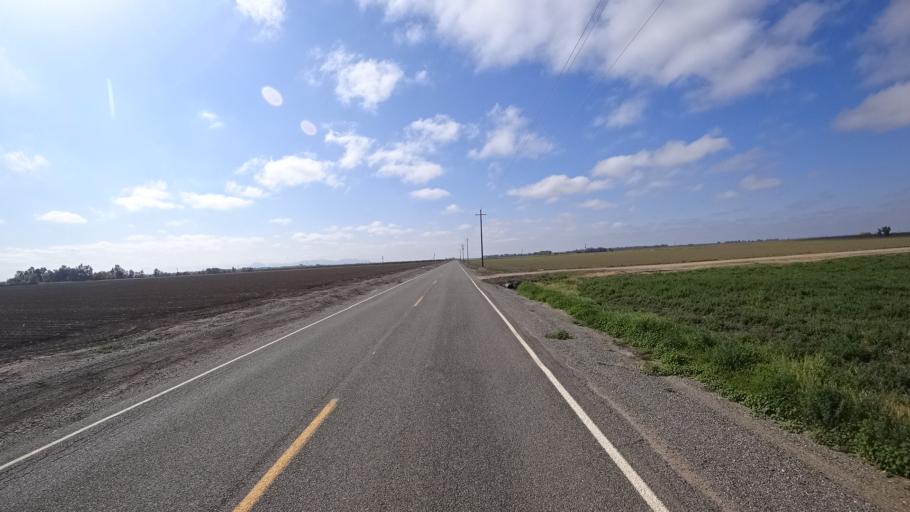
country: US
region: California
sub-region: Butte County
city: Biggs
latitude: 39.4244
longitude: -121.9295
